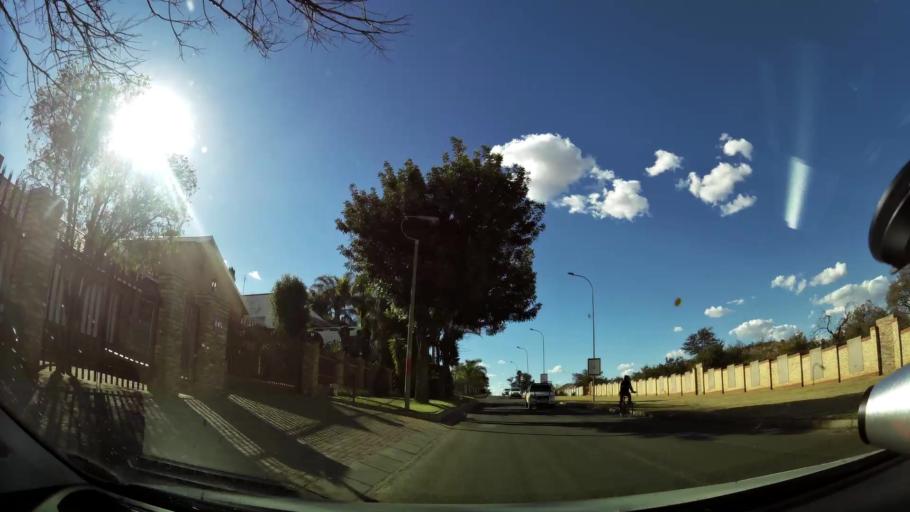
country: ZA
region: North-West
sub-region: Dr Kenneth Kaunda District Municipality
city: Klerksdorp
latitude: -26.8236
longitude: 26.6784
